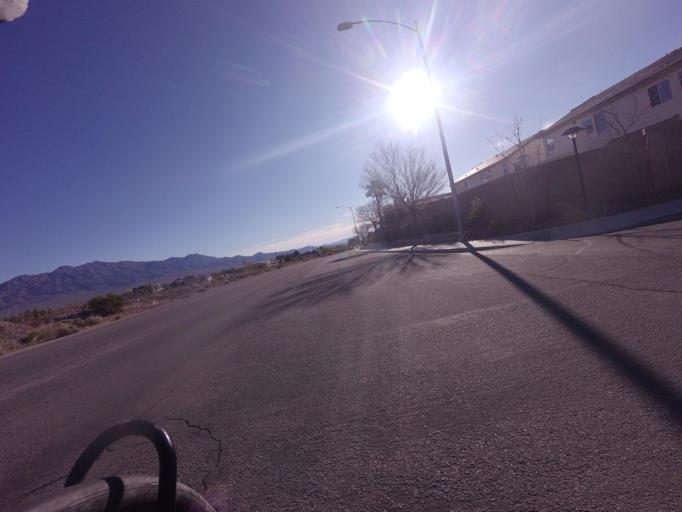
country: US
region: Nevada
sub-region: Clark County
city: Summerlin South
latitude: 36.3287
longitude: -115.2900
